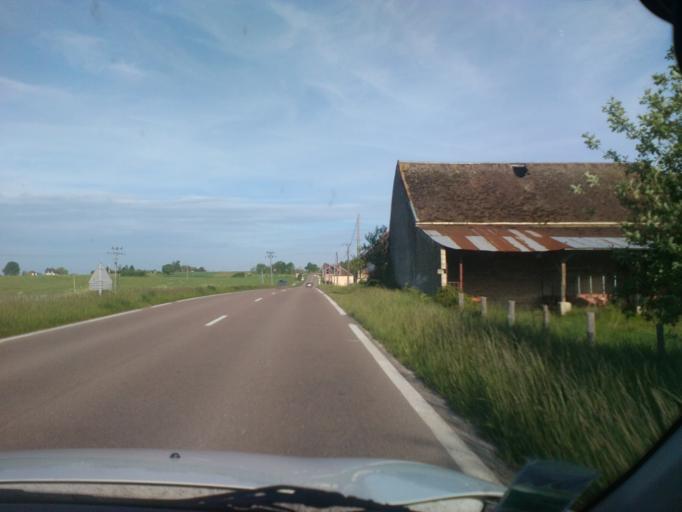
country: FR
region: Champagne-Ardenne
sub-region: Departement de l'Aube
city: Vendeuvre-sur-Barse
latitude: 48.2349
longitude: 4.3964
